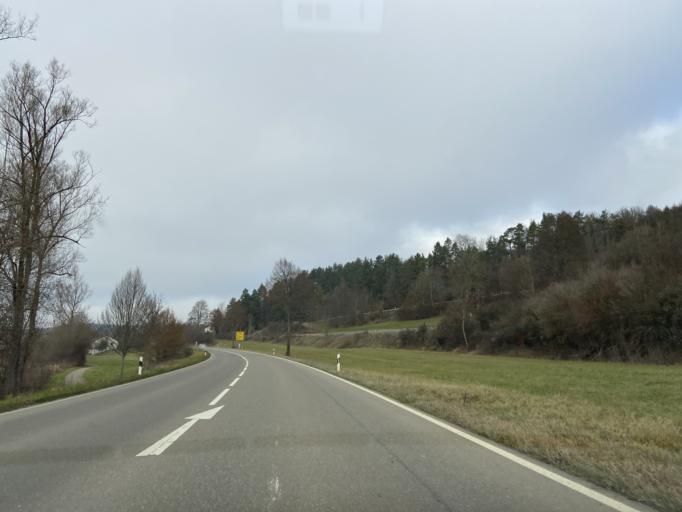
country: DE
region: Baden-Wuerttemberg
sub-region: Tuebingen Region
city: Gammertingen
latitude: 48.2419
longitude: 9.2260
